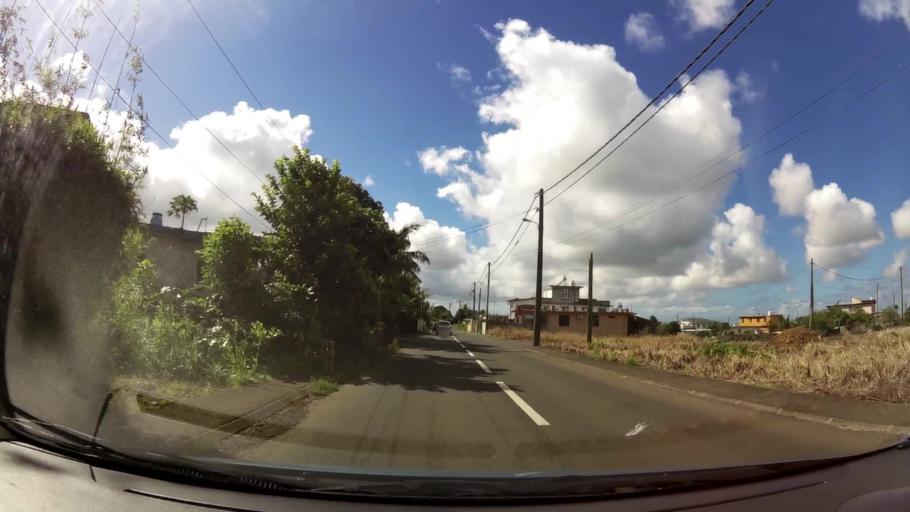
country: MU
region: Grand Port
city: Rose Belle
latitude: -20.3971
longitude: 57.5905
